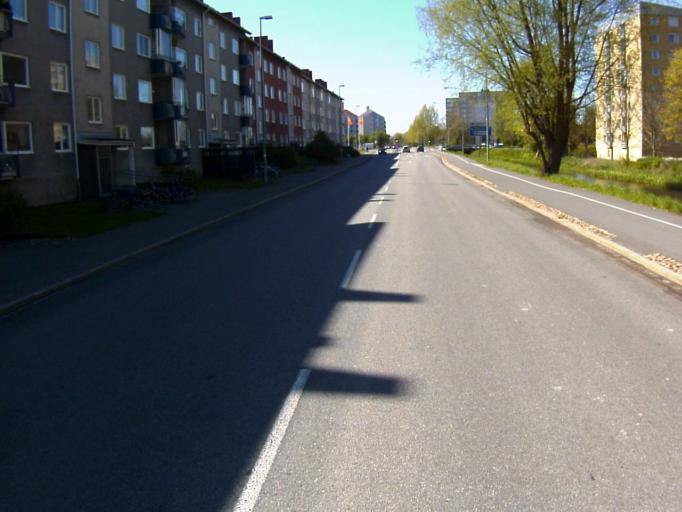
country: SE
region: Skane
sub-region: Kristianstads Kommun
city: Kristianstad
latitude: 56.0409
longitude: 14.1630
